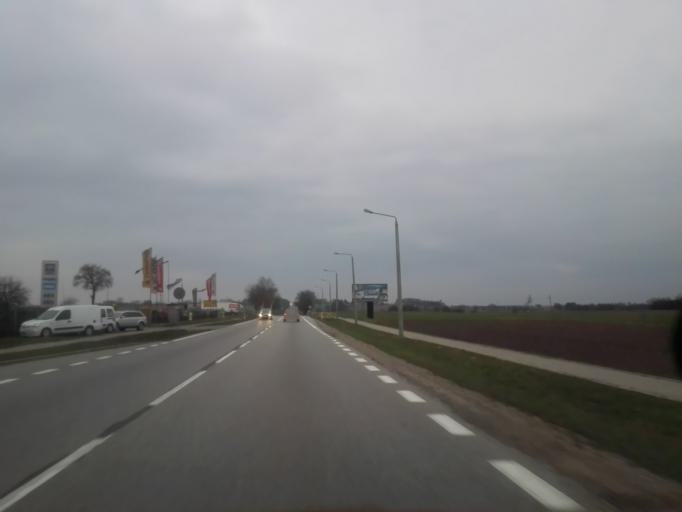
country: PL
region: Podlasie
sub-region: Powiat lomzynski
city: Piatnica
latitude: 53.2439
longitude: 22.1176
